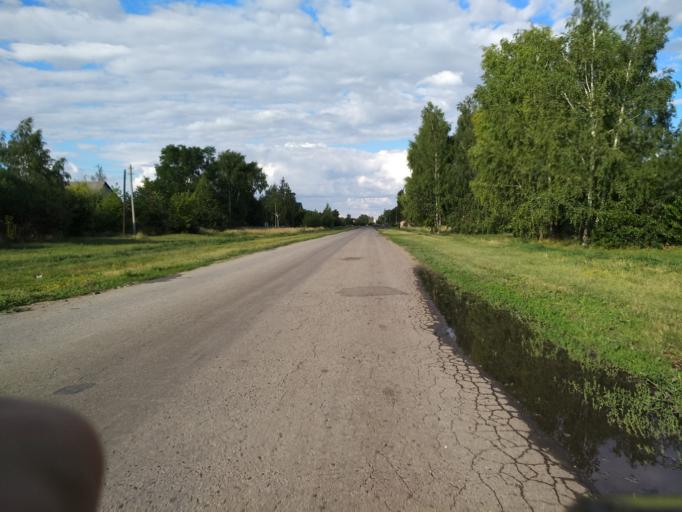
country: RU
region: Lipetsk
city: Dobrinka
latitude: 52.0363
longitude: 40.5266
